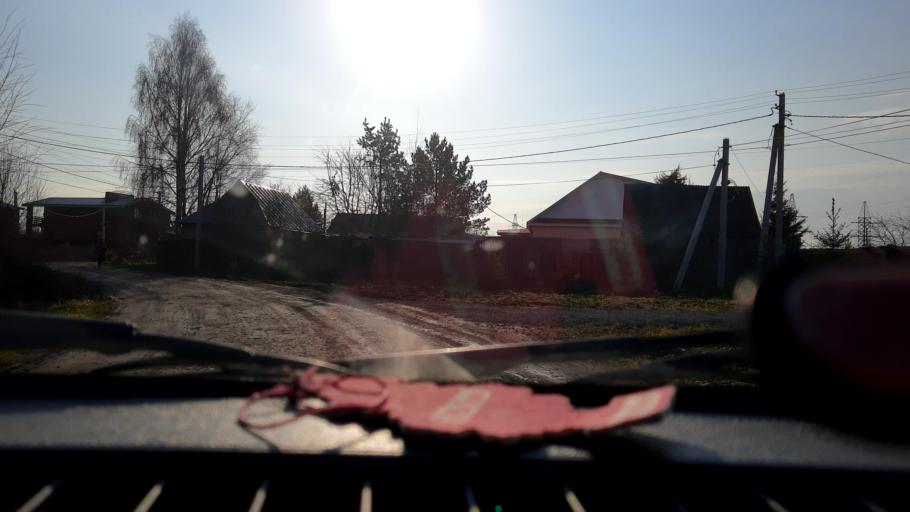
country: RU
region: Bashkortostan
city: Ufa
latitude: 54.6760
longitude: 56.0855
